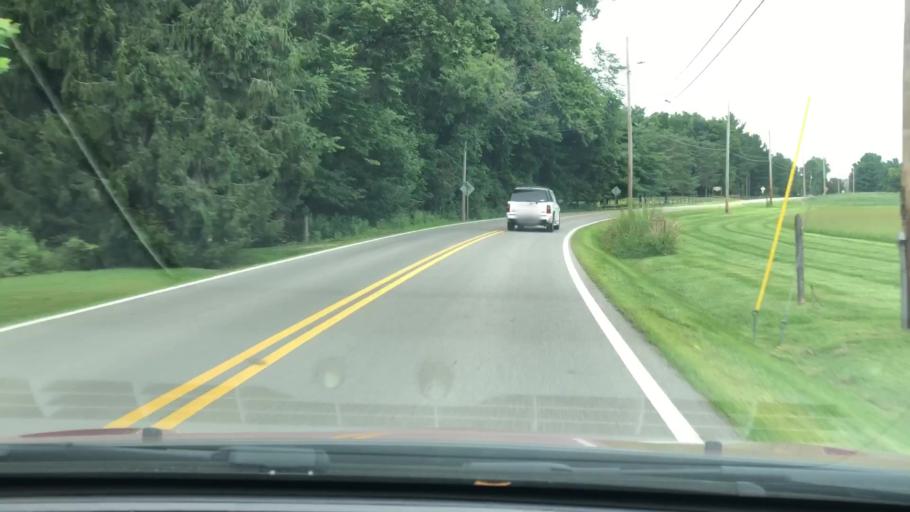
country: US
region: Ohio
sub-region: Delaware County
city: Sunbury
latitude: 40.1799
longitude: -82.8456
